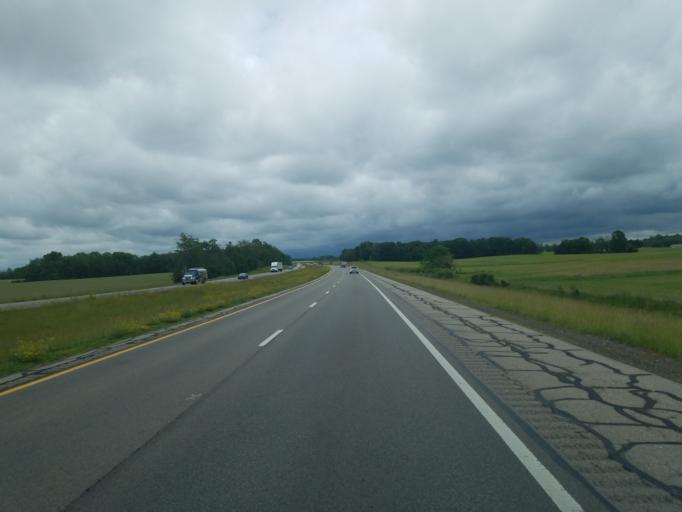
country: US
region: Ohio
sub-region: Crawford County
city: Crestline
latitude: 40.7619
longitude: -82.7197
